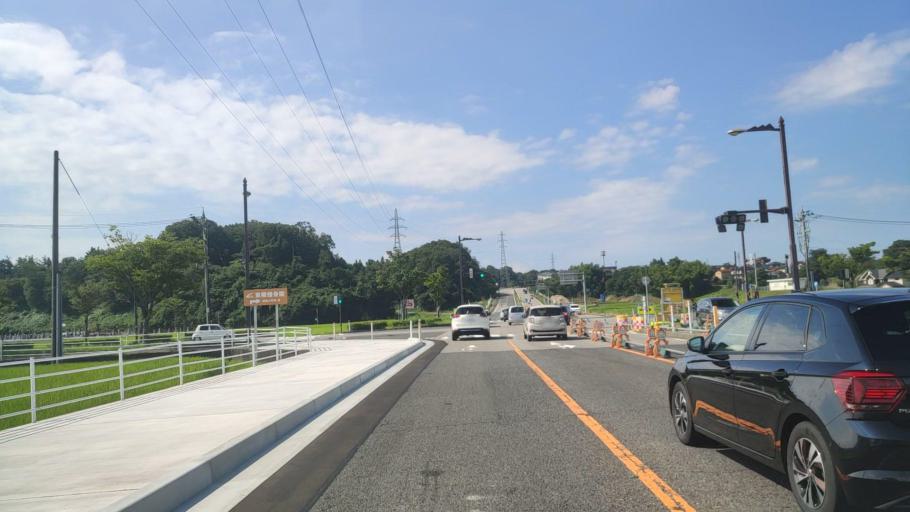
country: JP
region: Ishikawa
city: Komatsu
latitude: 36.4009
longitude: 136.5068
